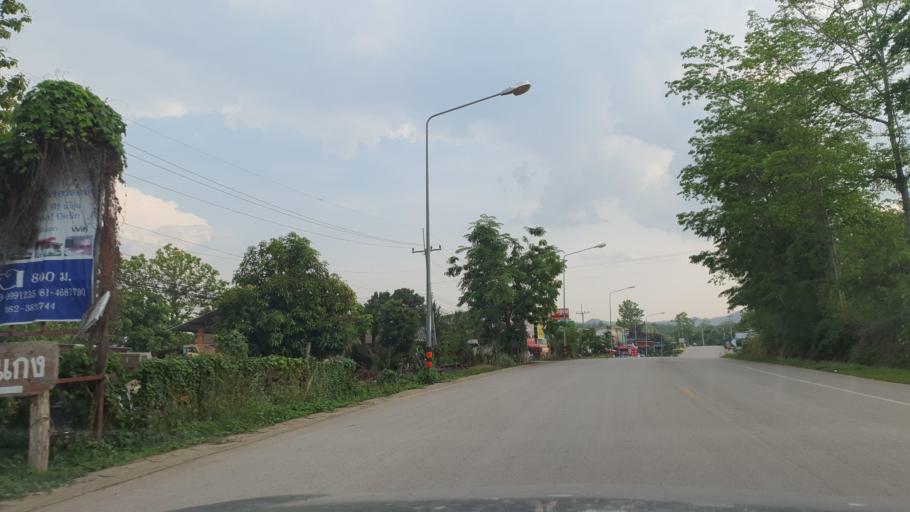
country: TH
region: Chiang Mai
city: Pai
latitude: 19.3488
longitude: 98.4349
